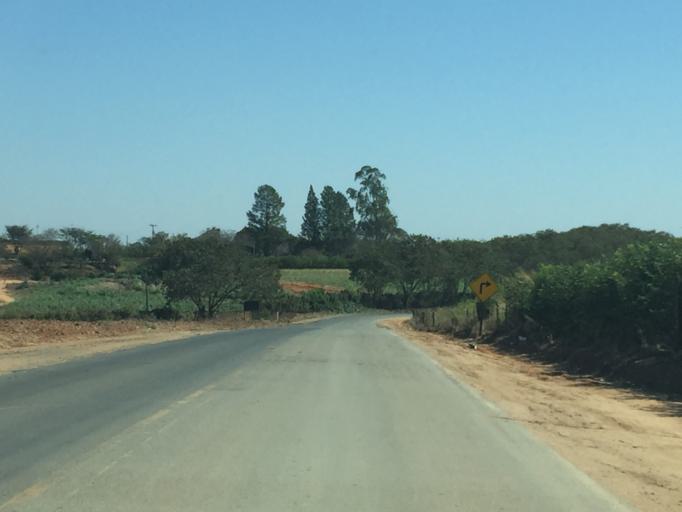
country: BR
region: Sao Paulo
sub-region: Itapira
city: Itapira
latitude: -22.4103
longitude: -46.8022
